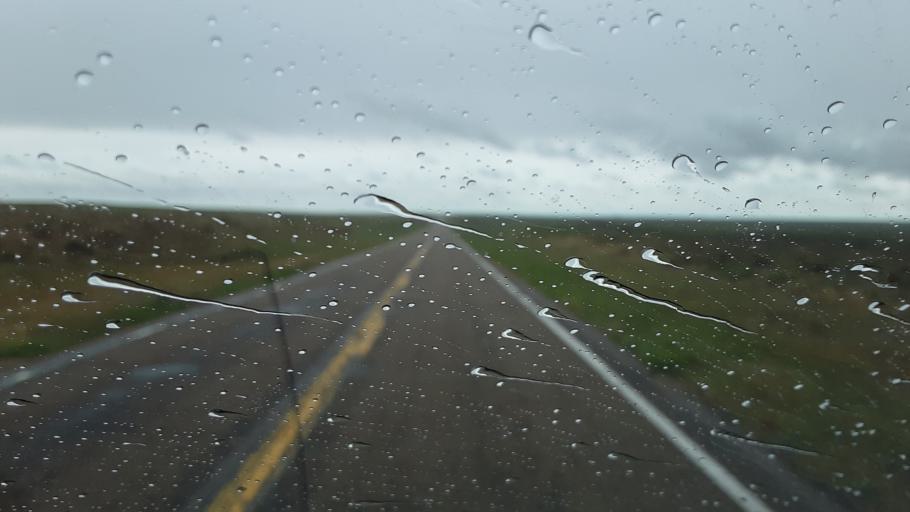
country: US
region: Colorado
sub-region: Lincoln County
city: Hugo
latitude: 38.8494
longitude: -103.2572
